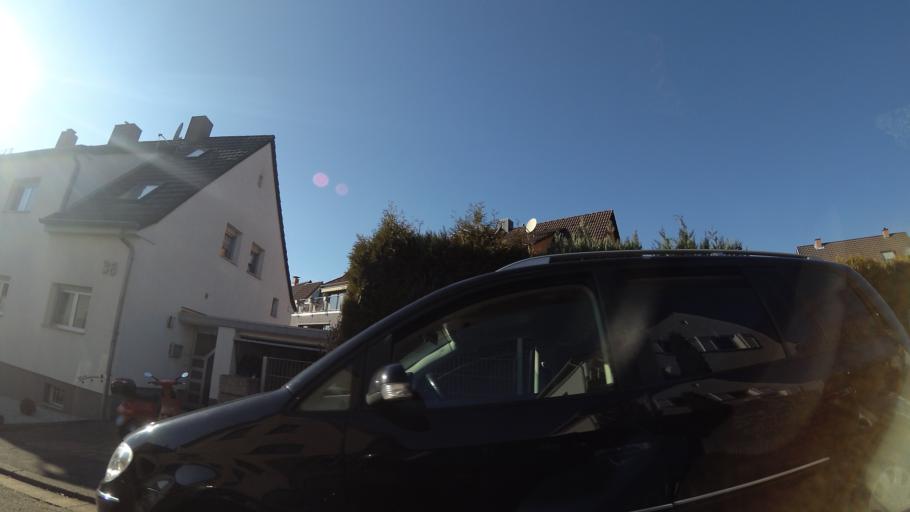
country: DE
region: Saarland
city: Sulzbach
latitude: 49.3113
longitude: 7.0671
